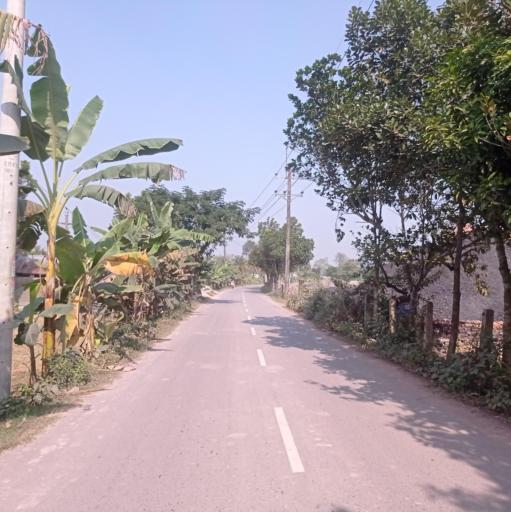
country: BD
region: Dhaka
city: Narsingdi
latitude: 24.0807
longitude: 90.6942
